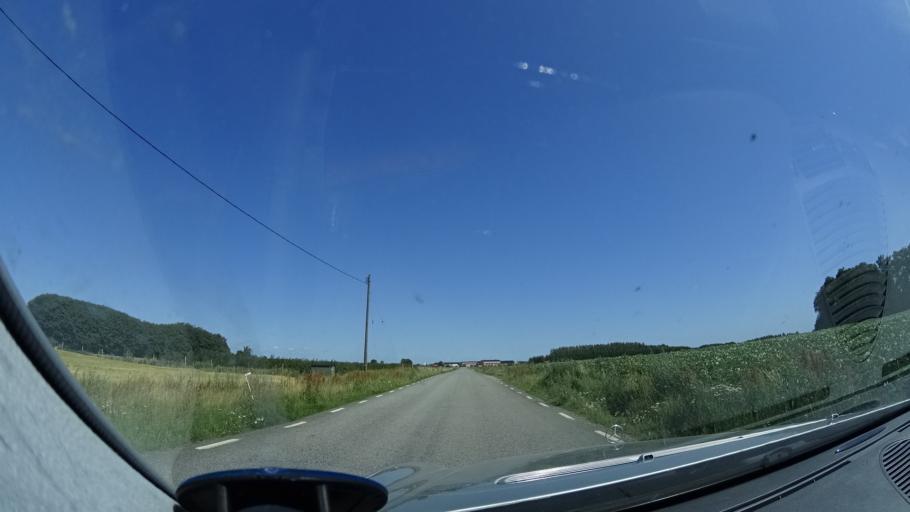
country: SE
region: Skane
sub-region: Kristianstads Kommun
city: Degeberga
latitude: 55.8890
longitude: 14.0334
